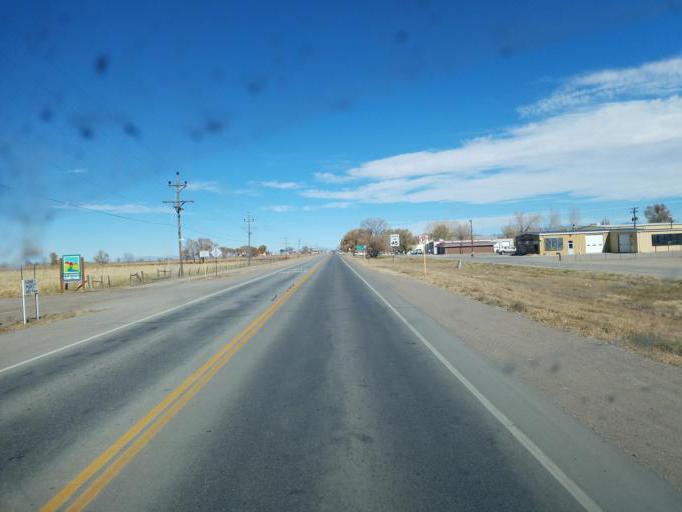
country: US
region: Colorado
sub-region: Alamosa County
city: Alamosa
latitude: 37.4745
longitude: -105.8574
